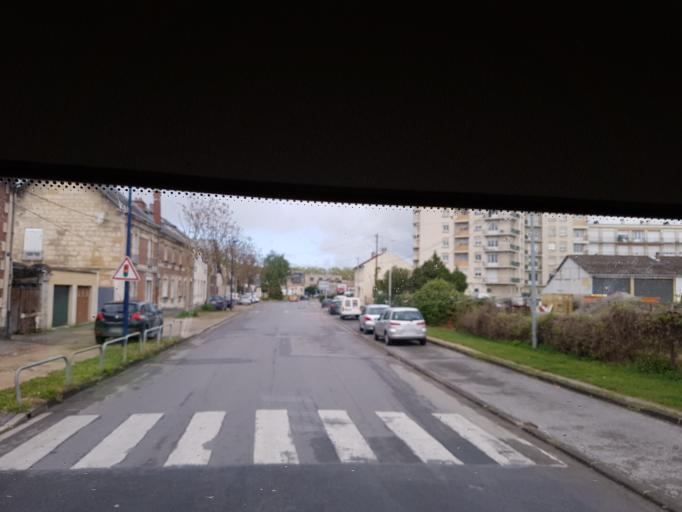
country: FR
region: Picardie
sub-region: Departement de l'Aisne
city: Soissons
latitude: 49.3853
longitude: 3.3350
